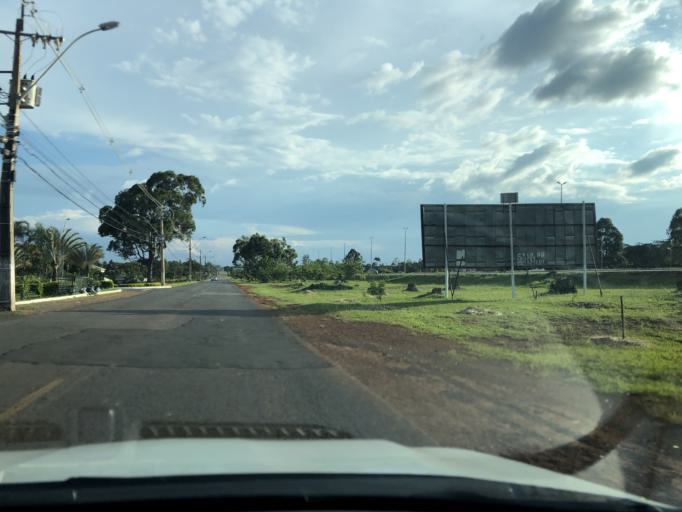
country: BR
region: Federal District
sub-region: Brasilia
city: Brasilia
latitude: -15.9132
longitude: -47.9683
